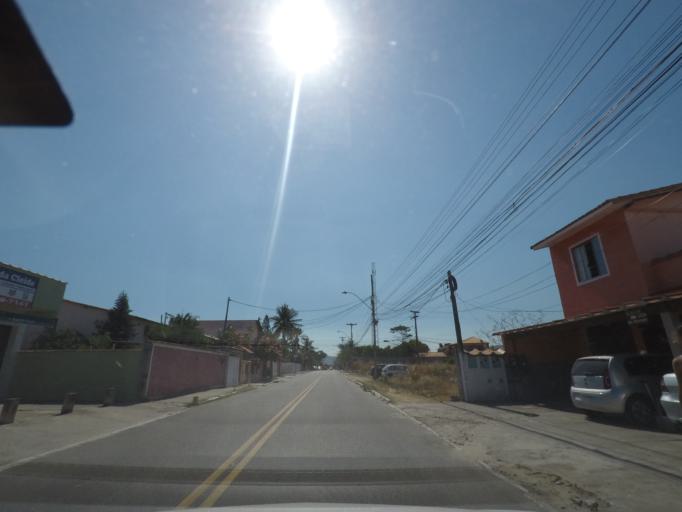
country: BR
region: Rio de Janeiro
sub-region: Marica
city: Marica
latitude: -22.9670
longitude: -42.9364
